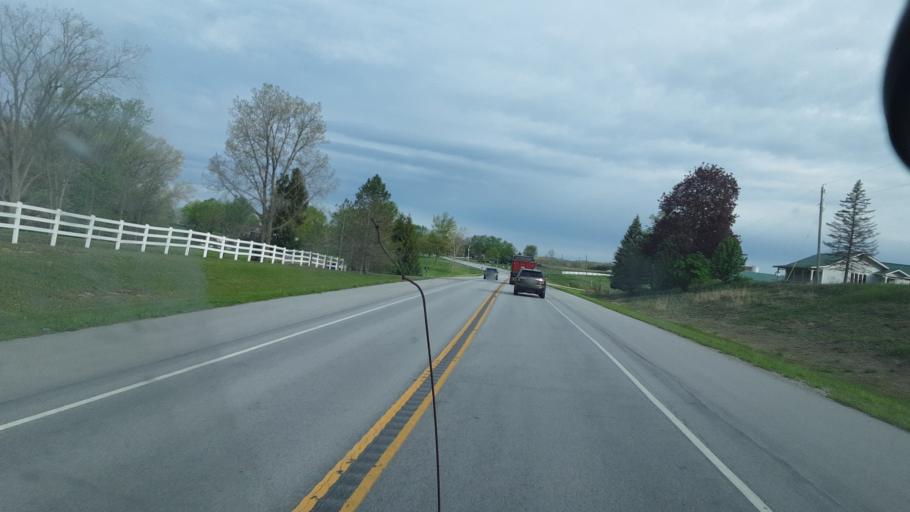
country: US
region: Indiana
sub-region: Whitley County
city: Churubusco
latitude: 41.2483
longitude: -85.3369
